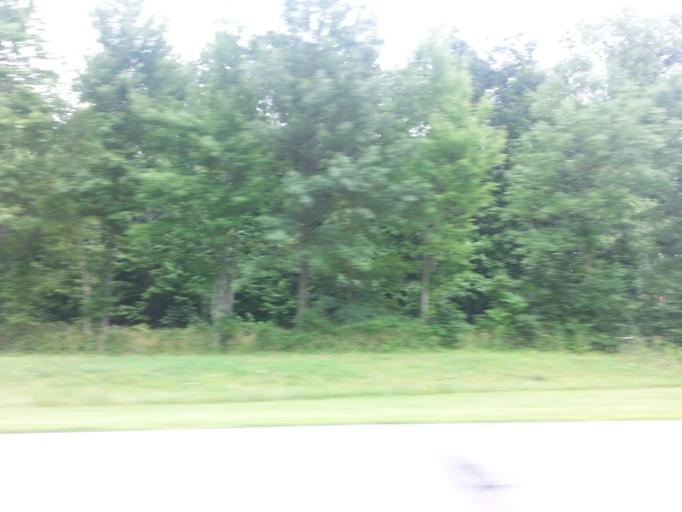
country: US
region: Ohio
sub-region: Brown County
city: Georgetown
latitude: 38.8919
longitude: -83.8966
